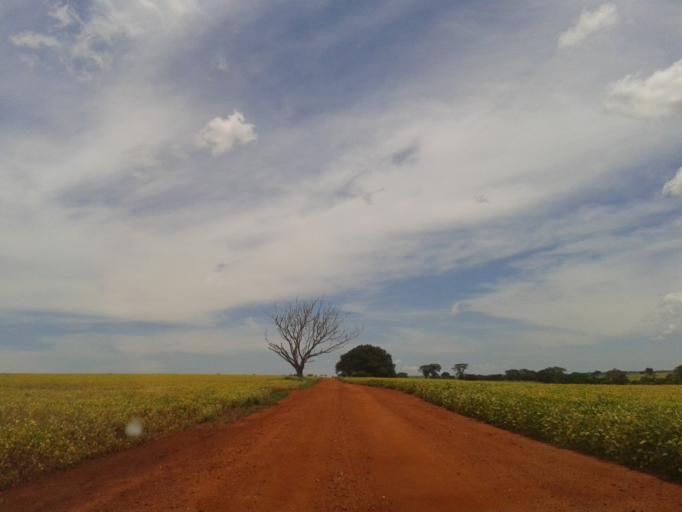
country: BR
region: Minas Gerais
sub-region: Capinopolis
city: Capinopolis
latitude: -18.6941
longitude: -49.7097
